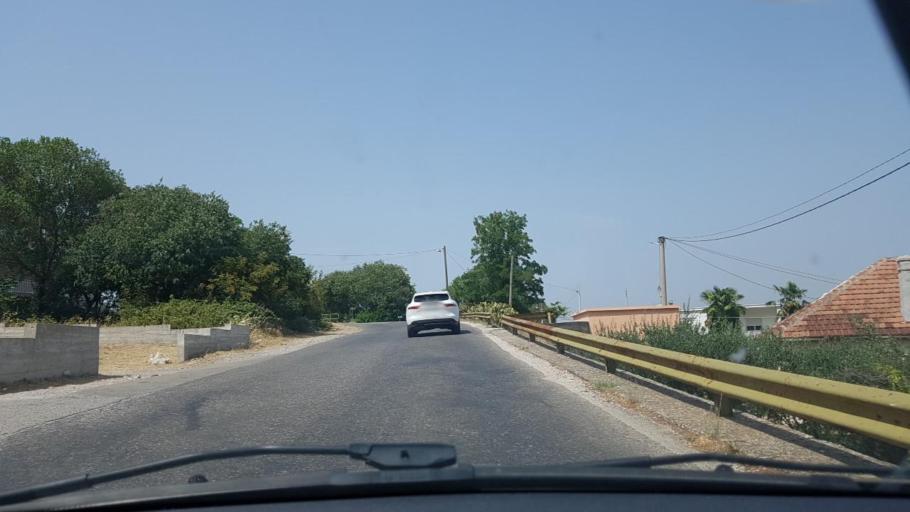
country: HR
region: Dubrovacko-Neretvanska
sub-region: Grad Dubrovnik
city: Metkovic
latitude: 43.0490
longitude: 17.7014
